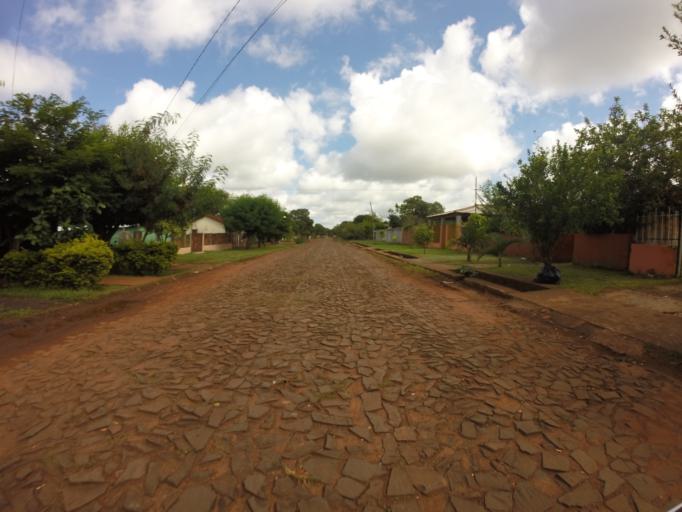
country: PY
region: Alto Parana
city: Ciudad del Este
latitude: -25.3984
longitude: -54.6476
